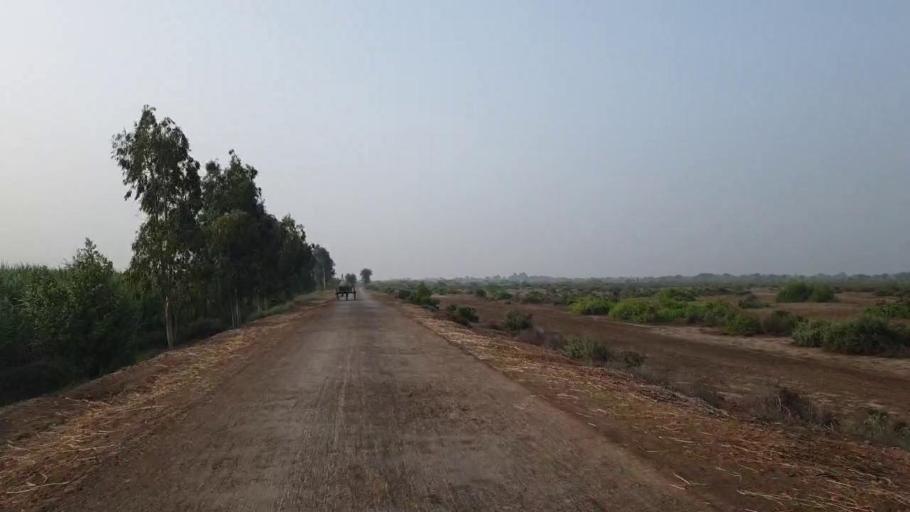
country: PK
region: Sindh
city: Tando Muhammad Khan
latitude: 25.1544
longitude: 68.6092
